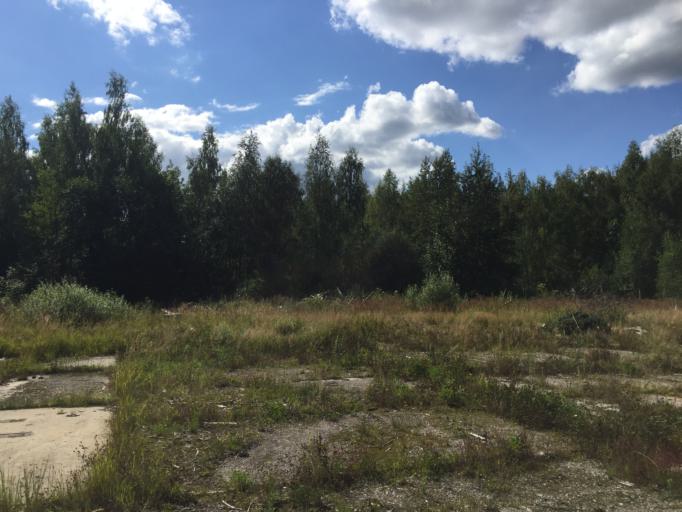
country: RU
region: Jaroslavl
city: Tunoshna
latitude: 57.5526
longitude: 40.1457
